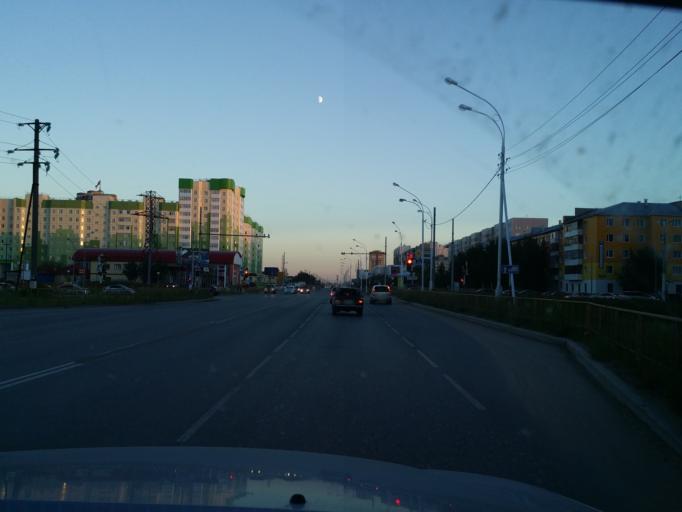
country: RU
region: Khanty-Mansiyskiy Avtonomnyy Okrug
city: Nizhnevartovsk
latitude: 60.9351
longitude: 76.6132
